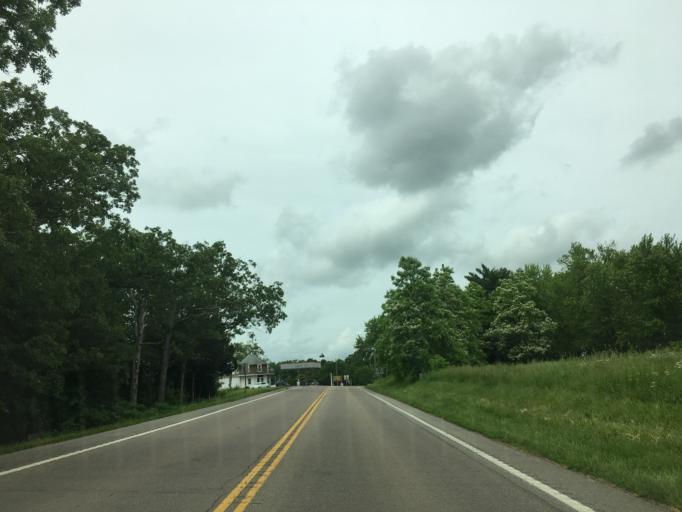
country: US
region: Missouri
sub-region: Gasconade County
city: Owensville
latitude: 38.4576
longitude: -91.4630
